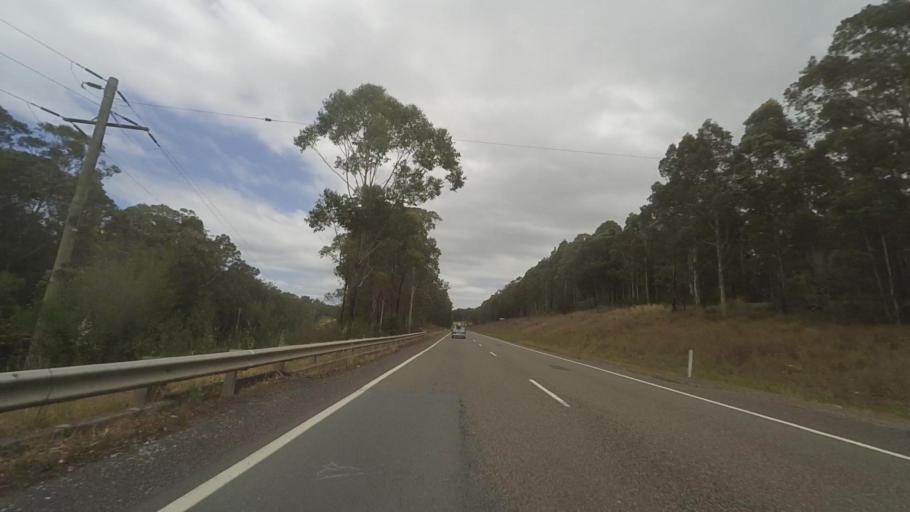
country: AU
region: New South Wales
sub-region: Shoalhaven Shire
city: Milton
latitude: -35.1290
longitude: 150.4701
